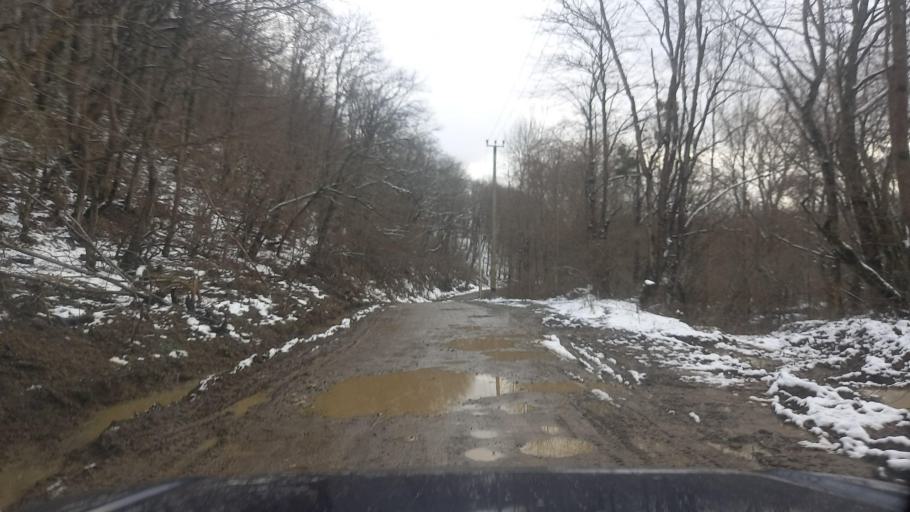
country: RU
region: Krasnodarskiy
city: Smolenskaya
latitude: 44.7011
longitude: 38.8271
